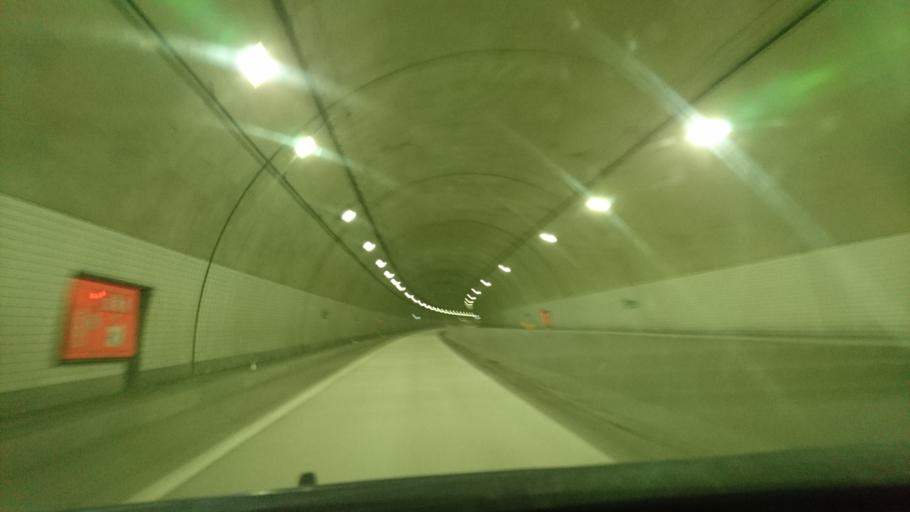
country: JP
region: Miyagi
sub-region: Oshika Gun
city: Onagawa Cho
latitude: 38.7004
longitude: 141.3790
